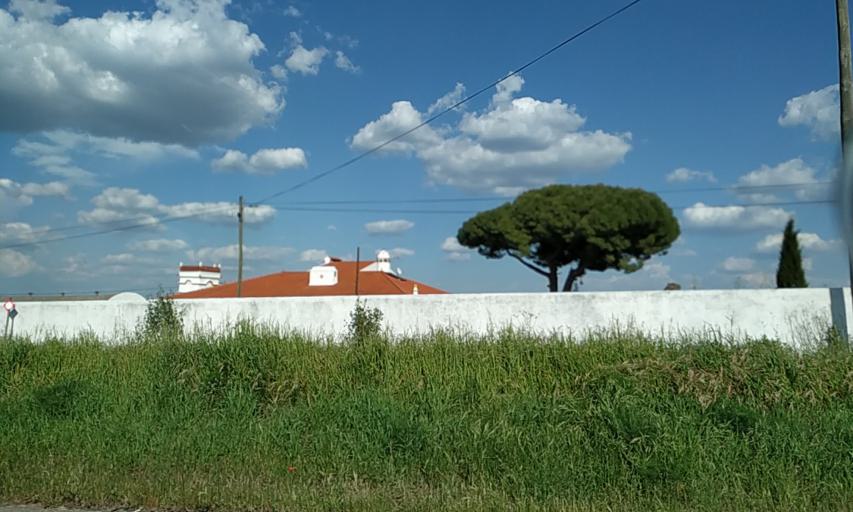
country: PT
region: Evora
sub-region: Estremoz
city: Estremoz
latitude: 38.8653
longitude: -7.5695
